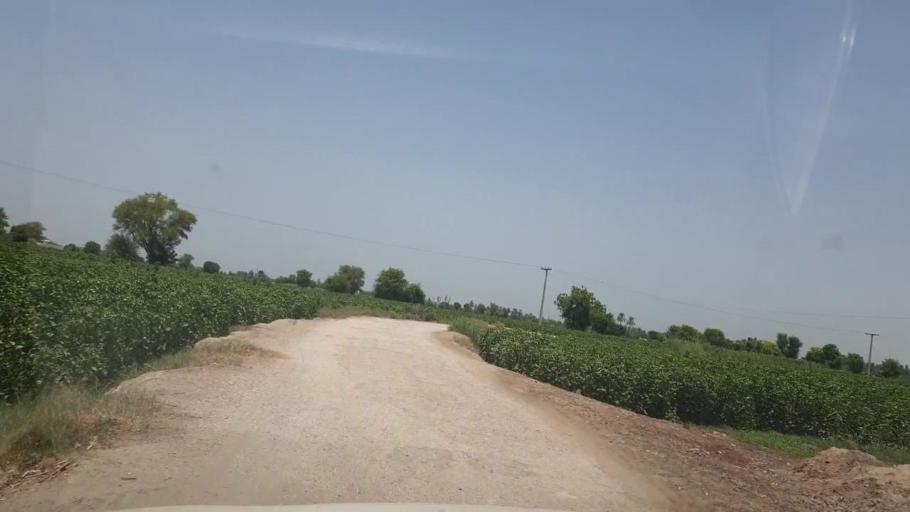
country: PK
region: Sindh
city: Bozdar
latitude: 27.1609
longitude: 68.6159
